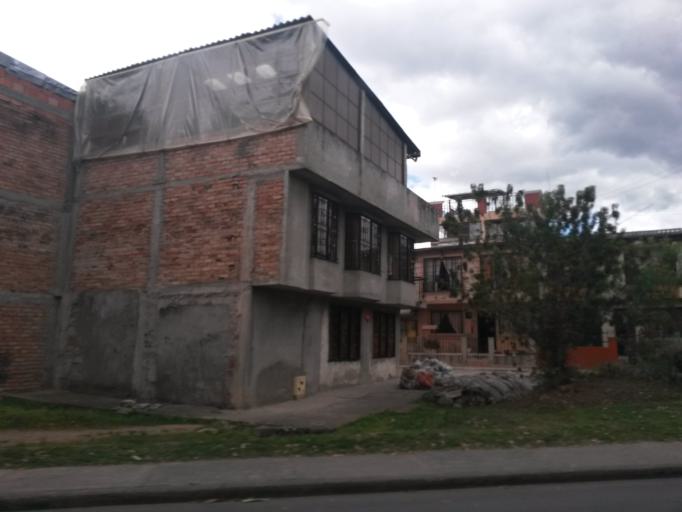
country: CO
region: Cauca
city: Popayan
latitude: 2.4382
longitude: -76.6187
